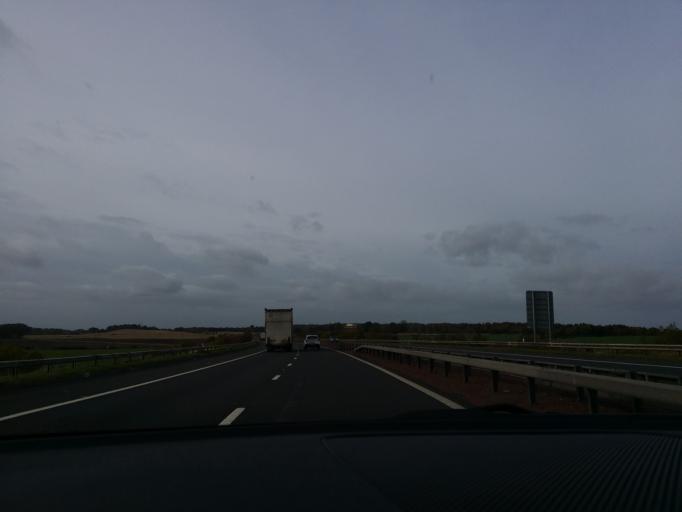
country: GB
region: Scotland
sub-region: West Lothian
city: Broxburn
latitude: 55.9665
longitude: -3.4485
